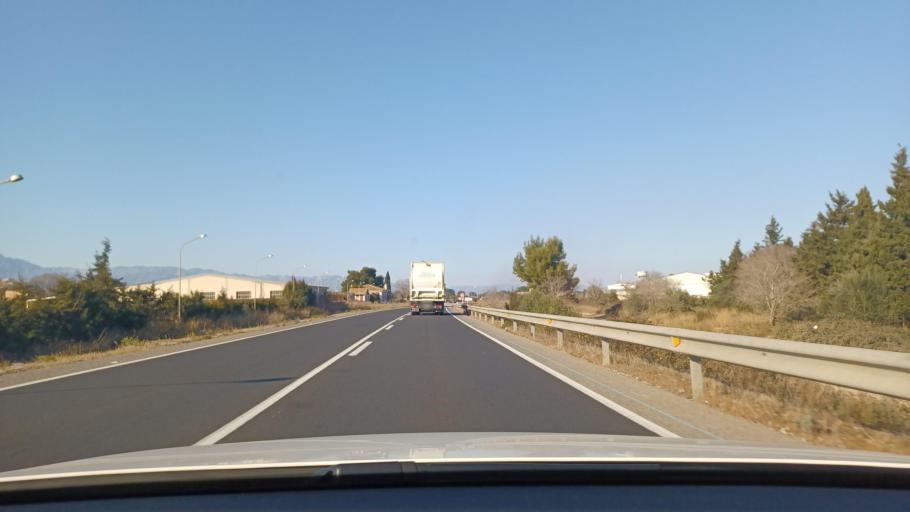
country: ES
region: Catalonia
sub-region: Provincia de Tarragona
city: Santa Barbara
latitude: 40.7135
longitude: 0.5064
